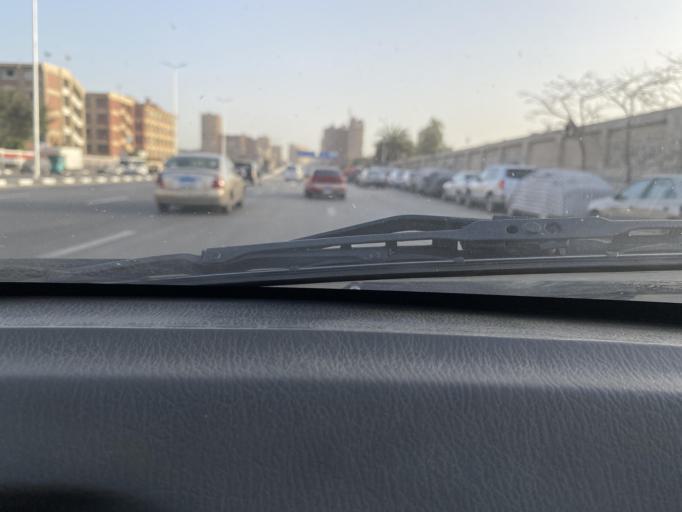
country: EG
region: Muhafazat al Qahirah
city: Cairo
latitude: 30.1175
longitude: 31.2966
